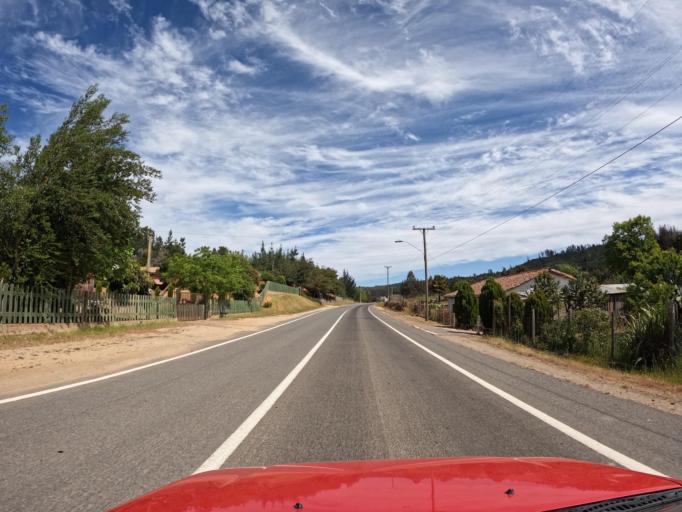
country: CL
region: Maule
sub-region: Provincia de Talca
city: Talca
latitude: -35.1410
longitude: -71.9632
